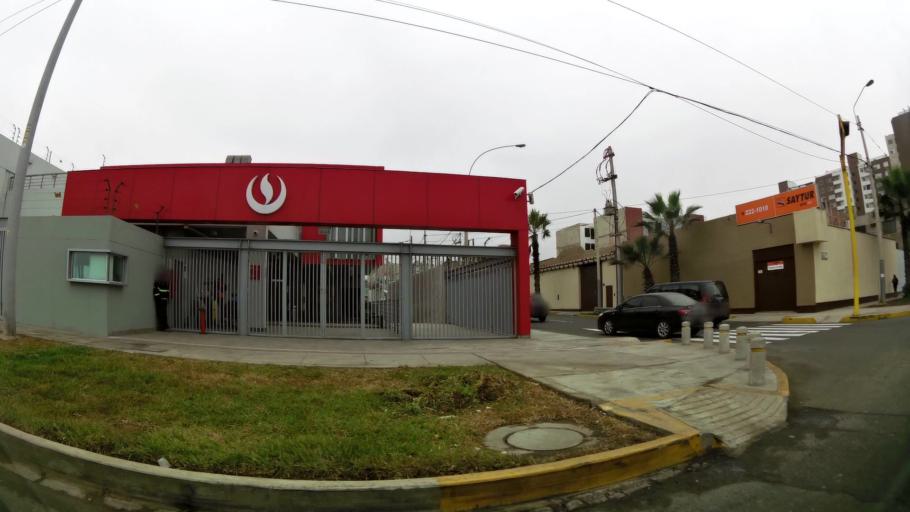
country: PE
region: Callao
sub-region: Callao
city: Callao
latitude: -12.0859
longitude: -77.0955
